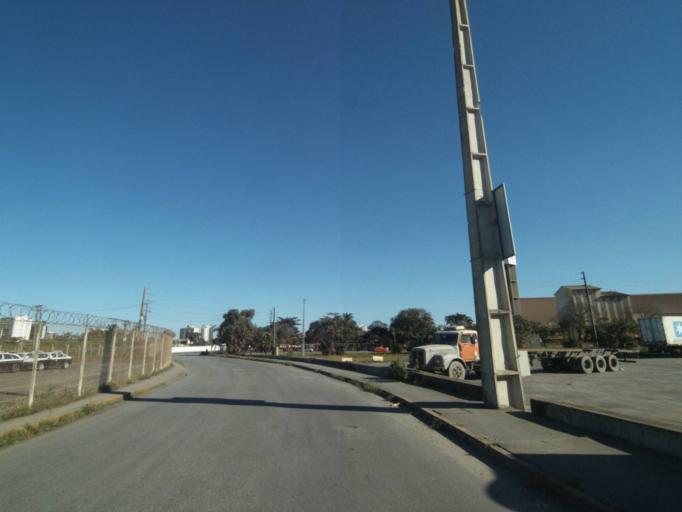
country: BR
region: Parana
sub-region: Paranagua
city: Paranagua
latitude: -25.5079
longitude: -48.5052
